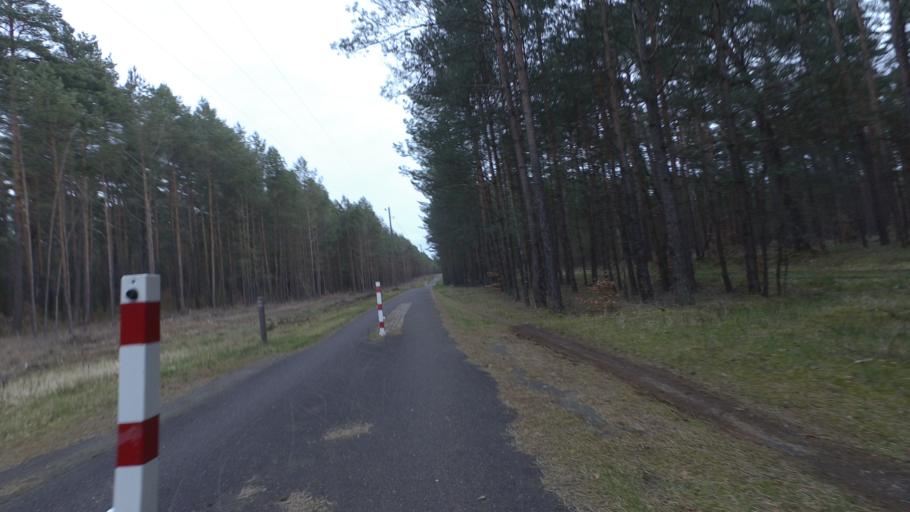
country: DE
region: Brandenburg
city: Neuruppin
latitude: 52.9854
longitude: 12.8740
